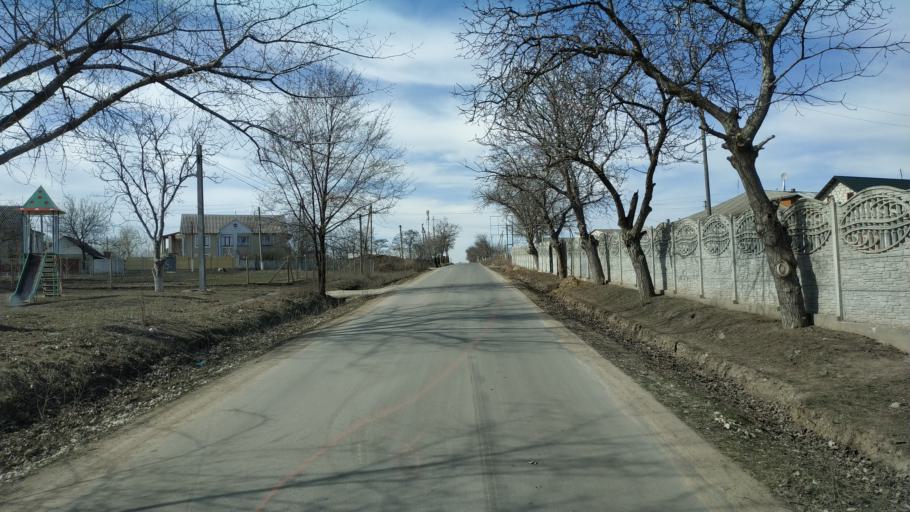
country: MD
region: Nisporeni
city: Nisporeni
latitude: 46.9632
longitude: 28.2097
